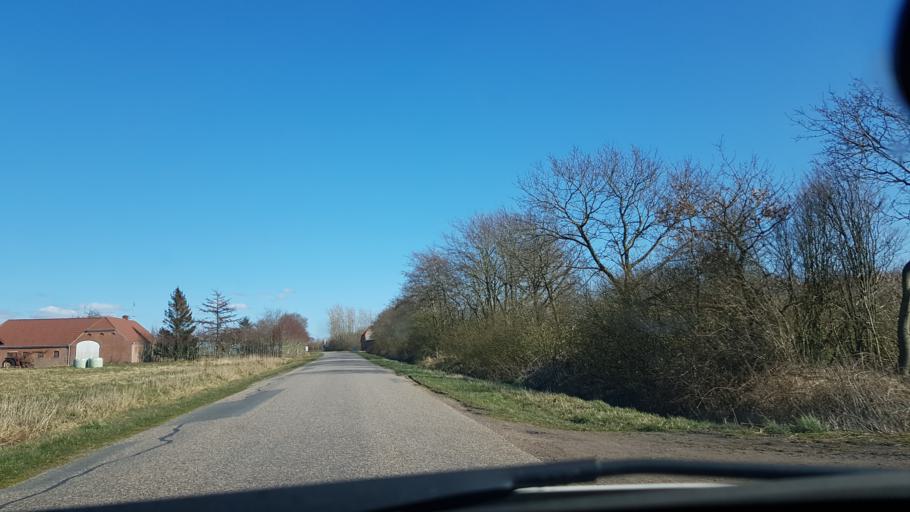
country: DK
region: South Denmark
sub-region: Tonder Kommune
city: Sherrebek
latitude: 55.2277
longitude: 8.7597
